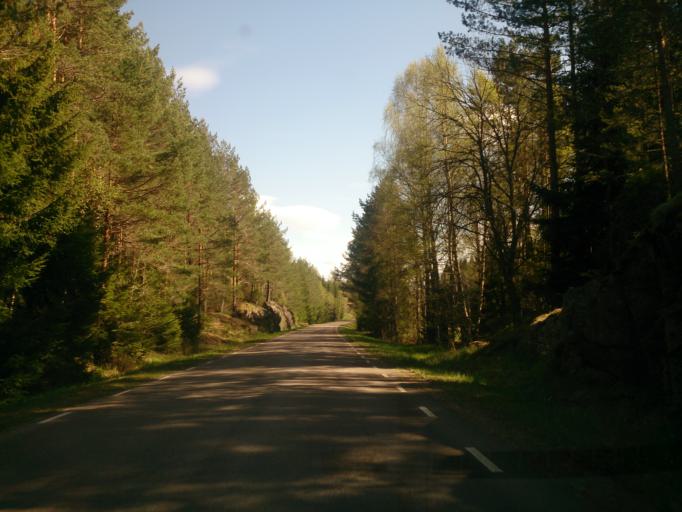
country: SE
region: OEstergoetland
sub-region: Linkopings Kommun
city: Ljungsbro
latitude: 58.6151
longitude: 15.4725
